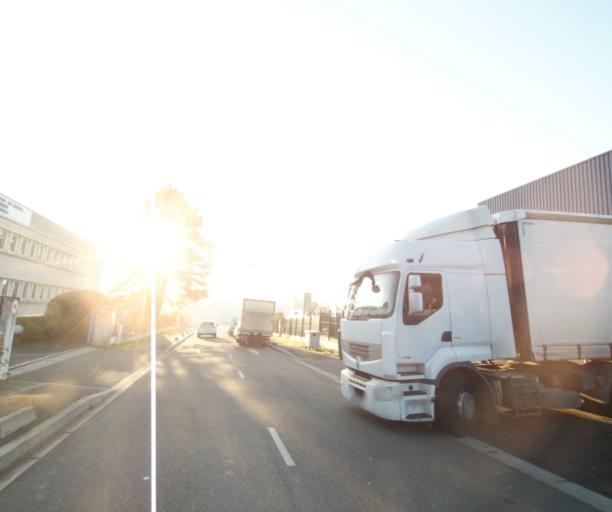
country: FR
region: Ile-de-France
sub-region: Departement du Val-d'Oise
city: Gonesse
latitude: 48.9888
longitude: 2.4559
